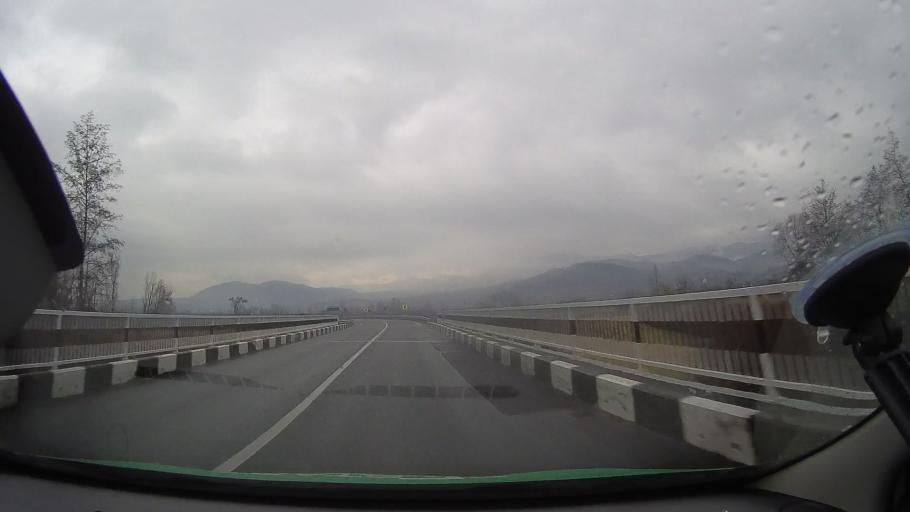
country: RO
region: Hunedoara
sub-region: Comuna Tomesti
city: Tomesti
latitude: 46.1817
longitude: 22.6603
